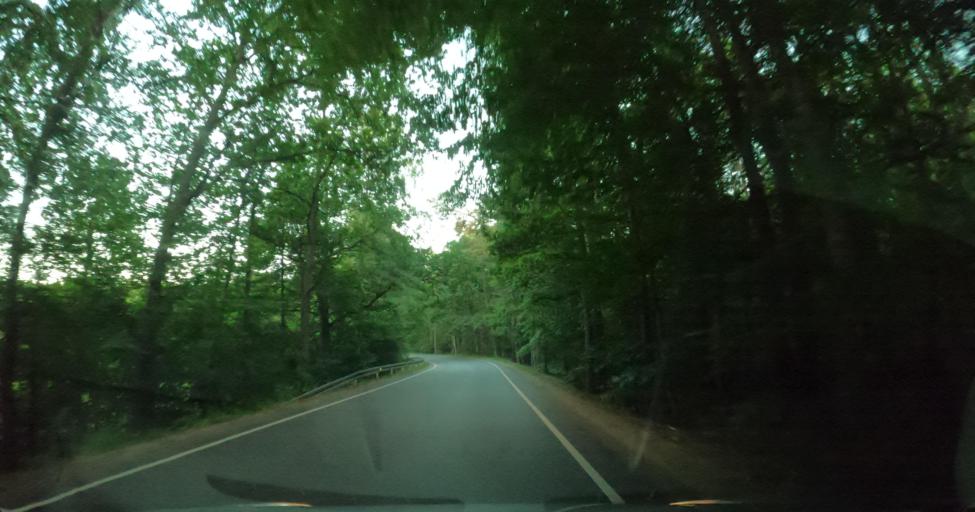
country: PL
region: Pomeranian Voivodeship
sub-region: Powiat leborski
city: Lebork
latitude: 54.5190
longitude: 17.7861
